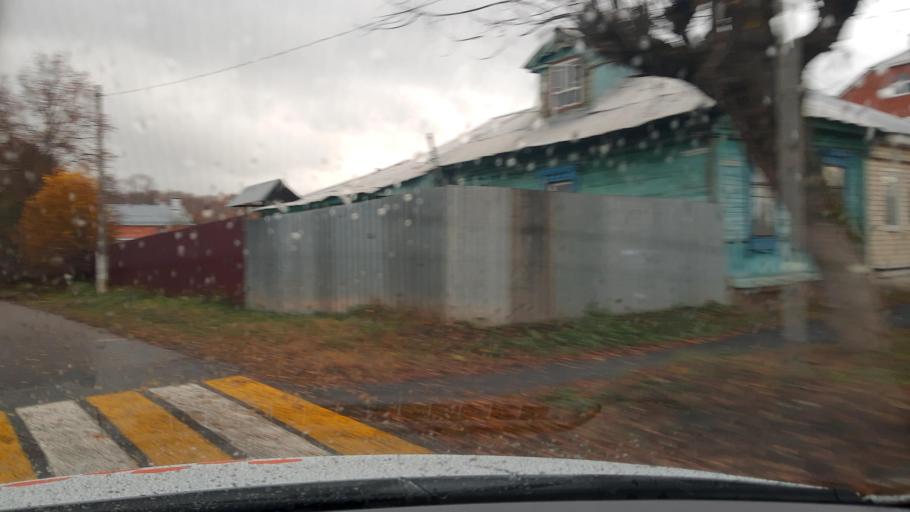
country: RU
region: Moskovskaya
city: Noginsk
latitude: 55.8491
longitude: 38.4158
